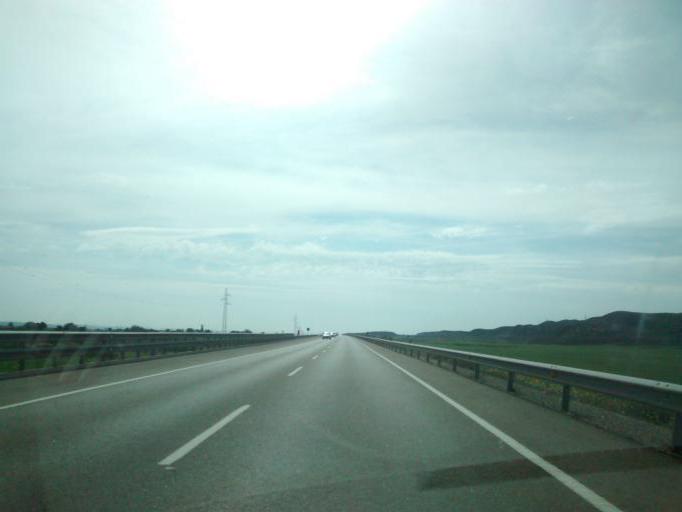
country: ES
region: Aragon
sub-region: Provincia de Zaragoza
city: El Burgo de Ebro
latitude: 41.5586
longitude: -0.7258
